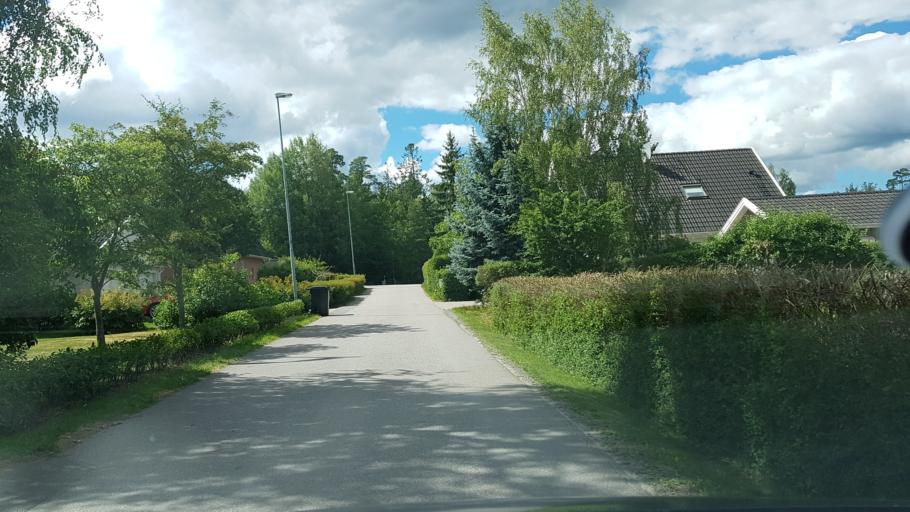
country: SE
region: Stockholm
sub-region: Upplands-Bro Kommun
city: Kungsaengen
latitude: 59.4778
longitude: 17.8023
